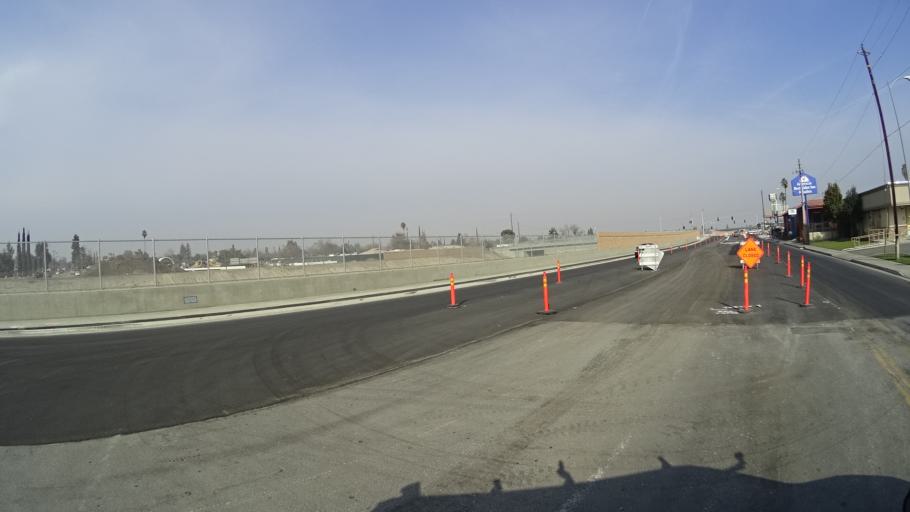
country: US
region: California
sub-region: Kern County
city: Bakersfield
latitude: 35.3449
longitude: -119.0389
